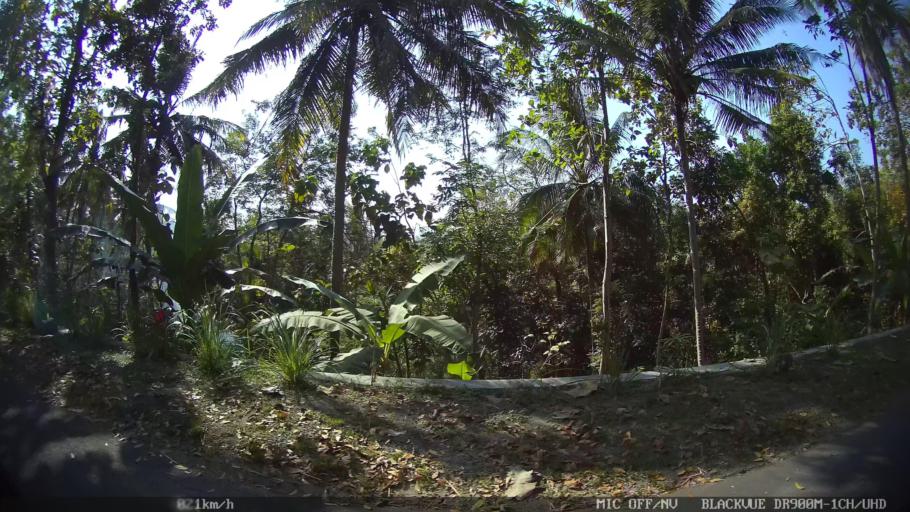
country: ID
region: Daerah Istimewa Yogyakarta
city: Kasihan
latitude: -7.8309
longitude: 110.2876
